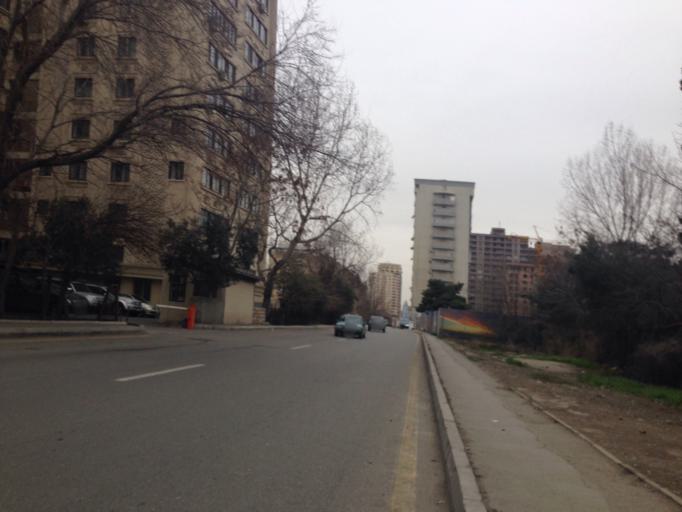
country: AZ
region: Baki
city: Baku
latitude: 40.3794
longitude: 49.8630
